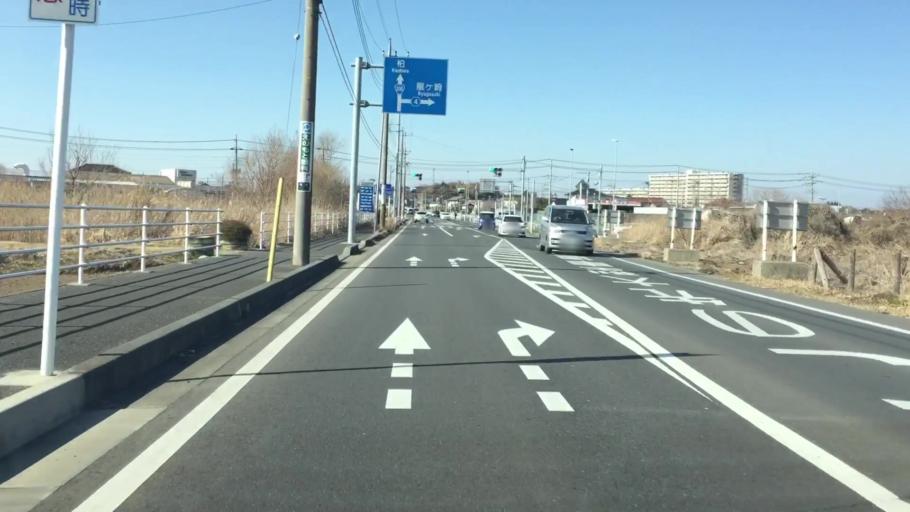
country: JP
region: Ibaraki
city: Ryugasaki
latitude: 35.8433
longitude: 140.1341
